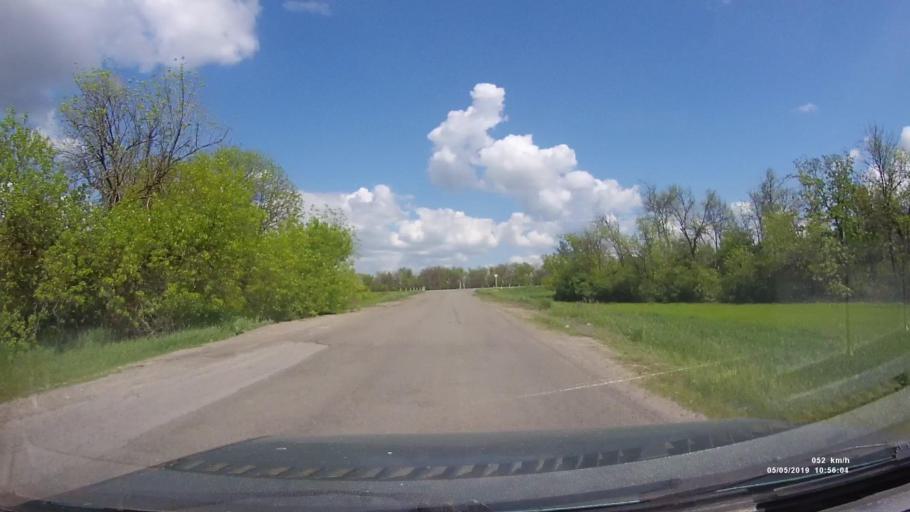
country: RU
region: Rostov
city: Ust'-Donetskiy
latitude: 47.6710
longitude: 40.8201
